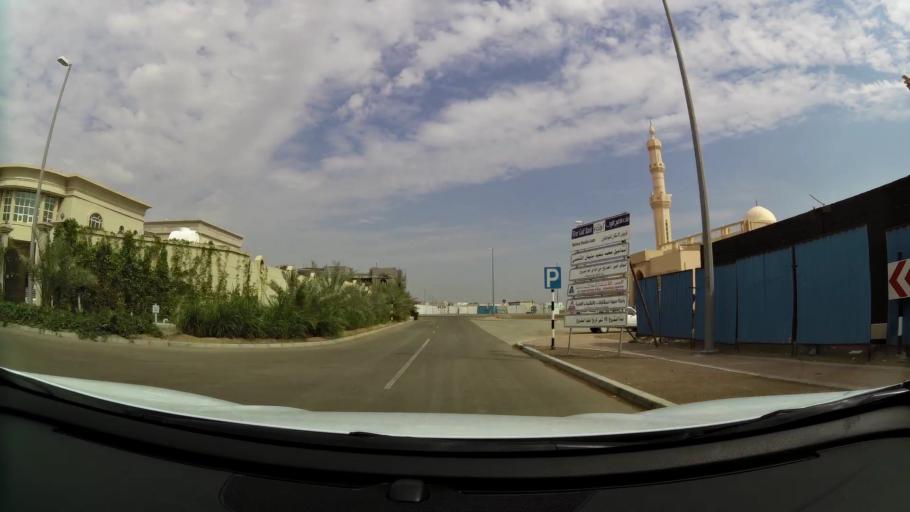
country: AE
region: Abu Dhabi
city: Al Ain
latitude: 24.1918
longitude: 55.8103
